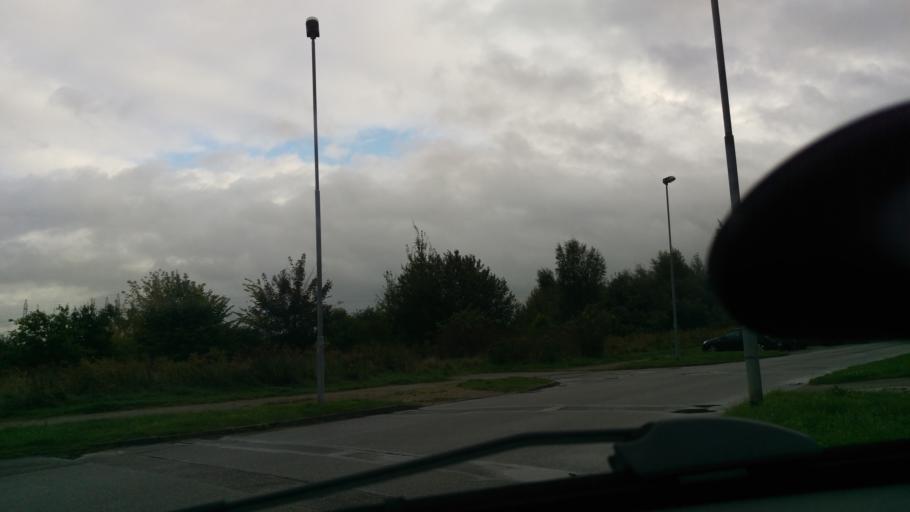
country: PL
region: West Pomeranian Voivodeship
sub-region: Szczecin
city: Szczecin
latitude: 53.3676
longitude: 14.6685
